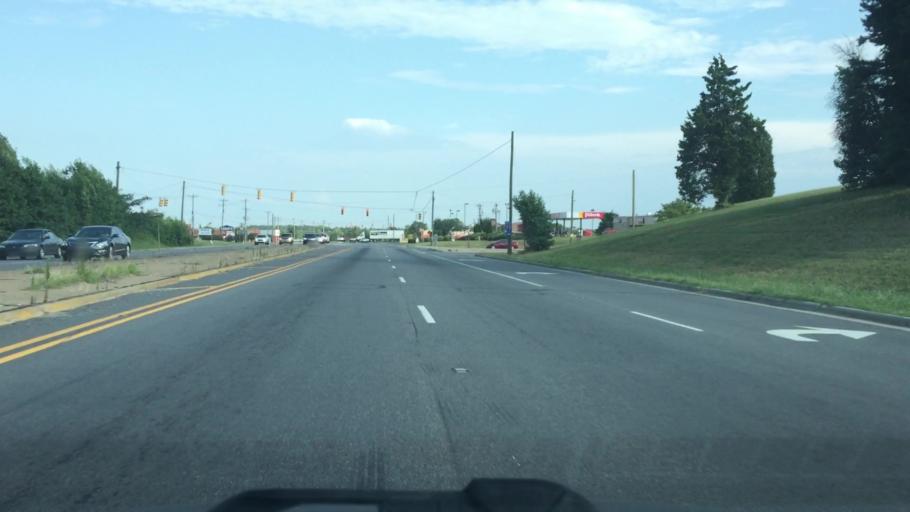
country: US
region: North Carolina
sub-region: Iredell County
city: Troutman
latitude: 35.6733
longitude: -80.8559
